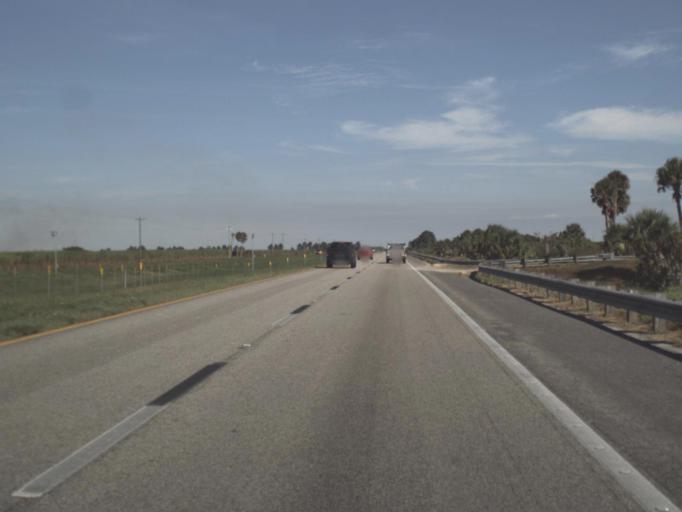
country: US
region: Florida
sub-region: Hendry County
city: Harlem
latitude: 26.7538
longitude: -81.0321
